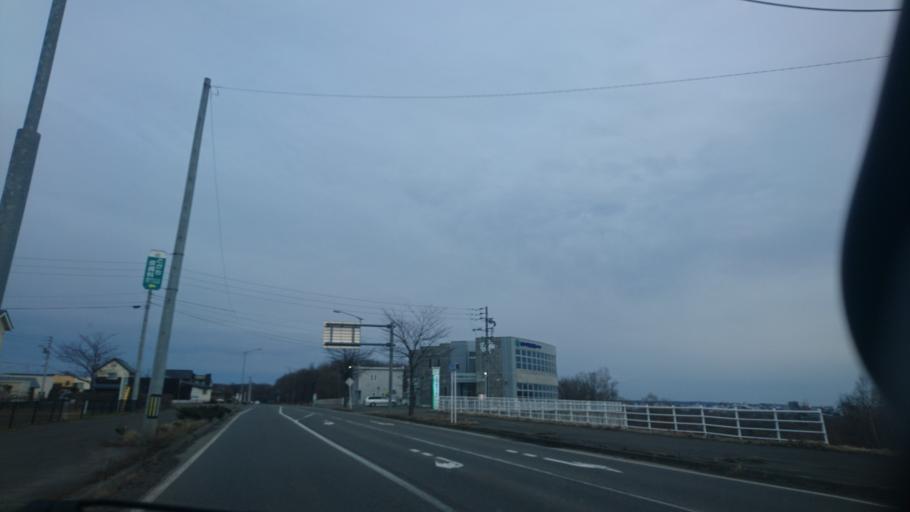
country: JP
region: Hokkaido
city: Obihiro
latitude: 42.9492
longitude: 143.1876
